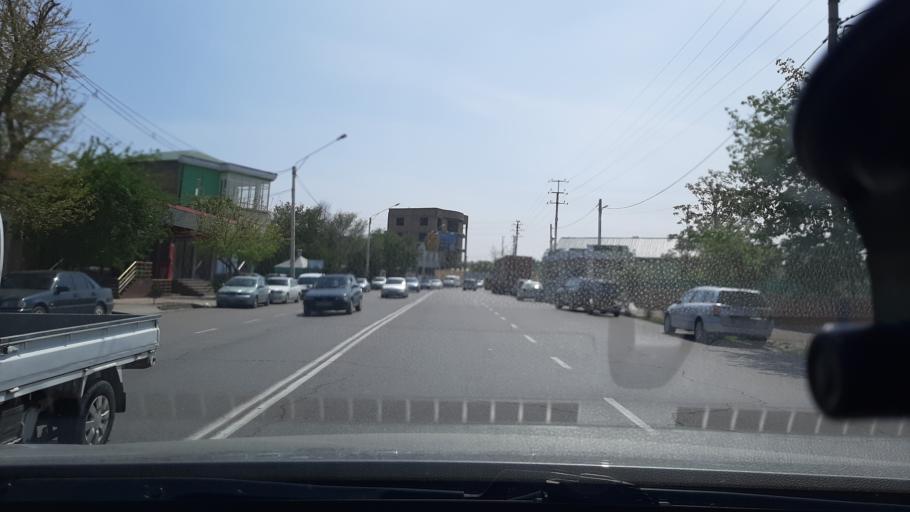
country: TJ
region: Viloyati Sughd
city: Khujand
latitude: 40.2885
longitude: 69.6420
